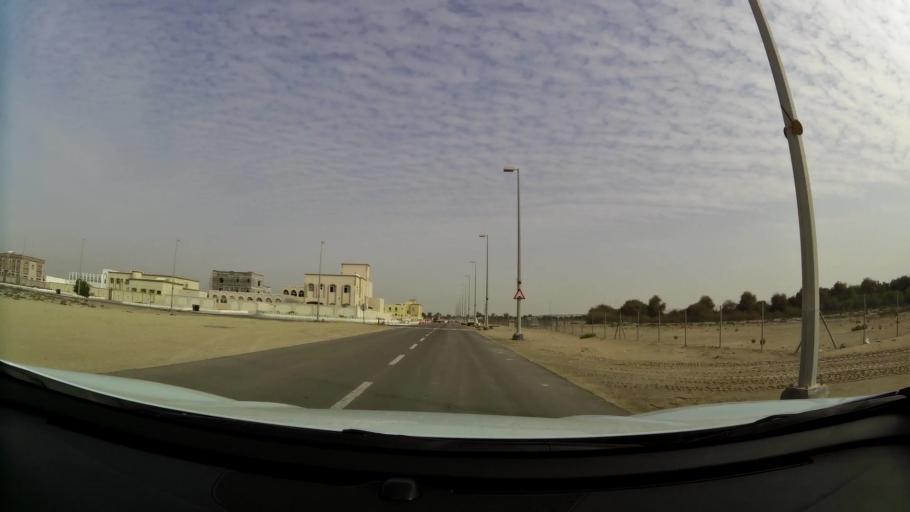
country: AE
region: Abu Dhabi
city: Abu Dhabi
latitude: 24.6175
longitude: 54.7084
